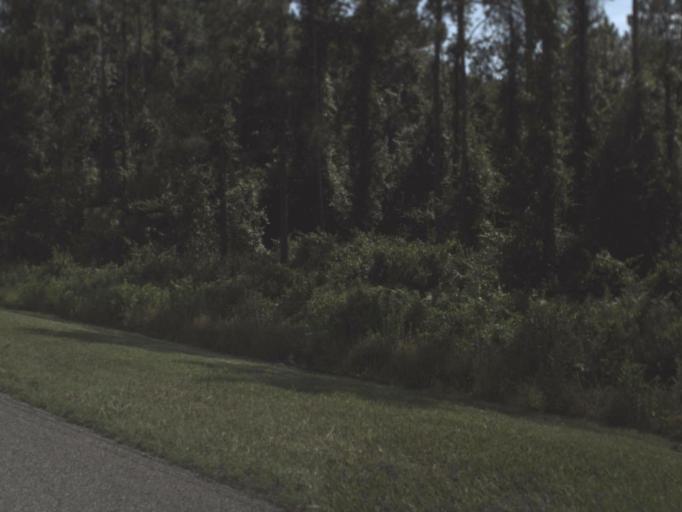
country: US
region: Florida
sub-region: Marion County
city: Citra
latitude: 29.4842
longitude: -82.1026
